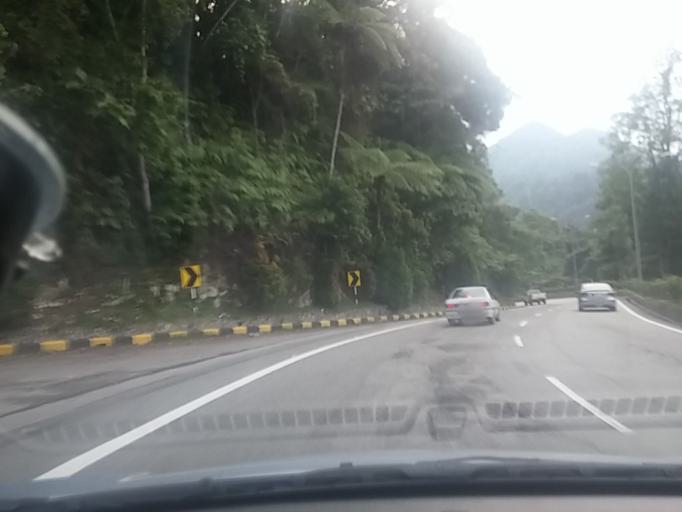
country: MY
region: Pahang
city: Kampung Bukit Tinggi, Bentong
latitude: 3.3693
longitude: 101.7764
